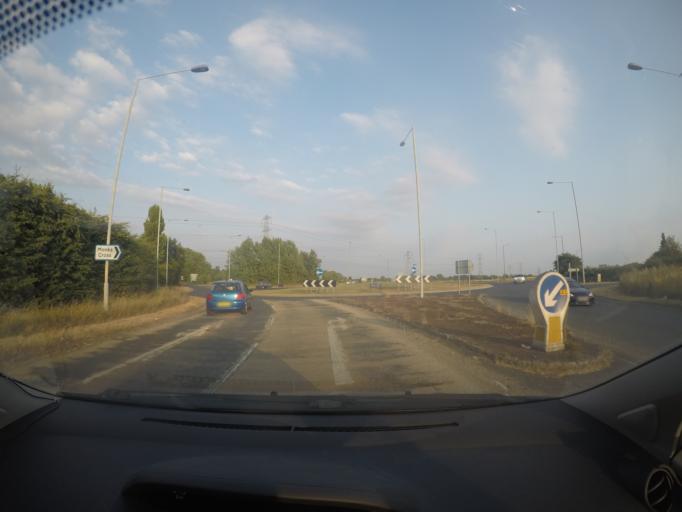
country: GB
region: England
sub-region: City of York
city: Huntington
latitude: 53.9993
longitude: -1.0434
